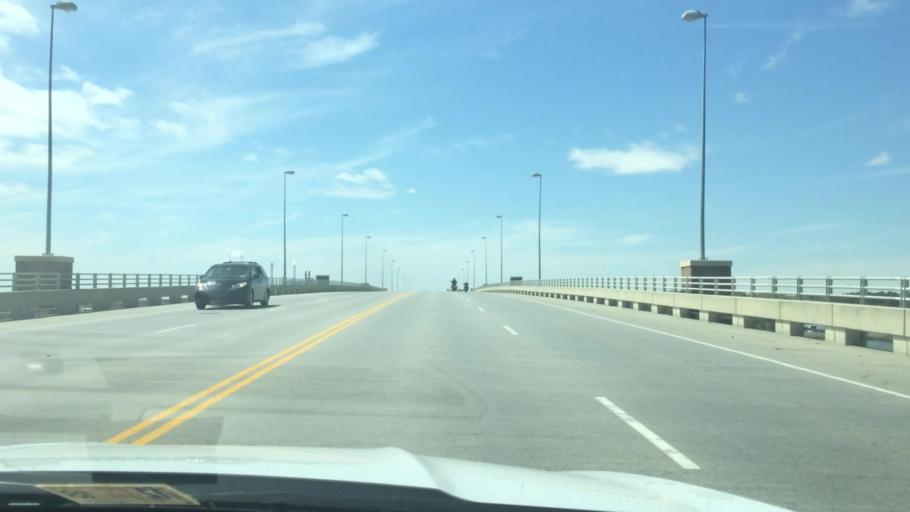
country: US
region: Virginia
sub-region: King William County
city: West Point
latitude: 37.5369
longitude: -76.7869
